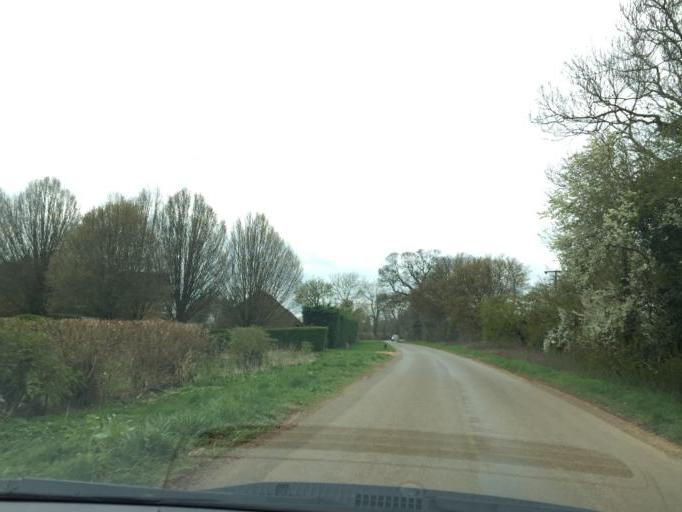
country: GB
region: England
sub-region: Oxfordshire
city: Hanwell
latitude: 52.1066
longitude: -1.4272
